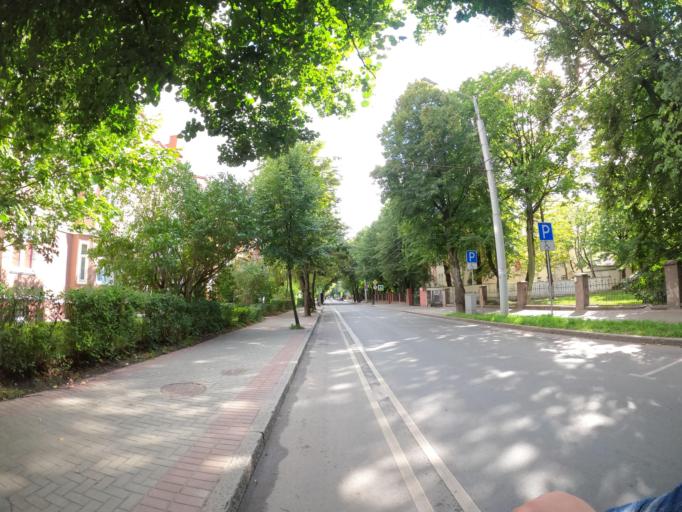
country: RU
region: Kaliningrad
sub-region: Gorod Kaliningrad
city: Kaliningrad
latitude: 54.7346
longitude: 20.4782
